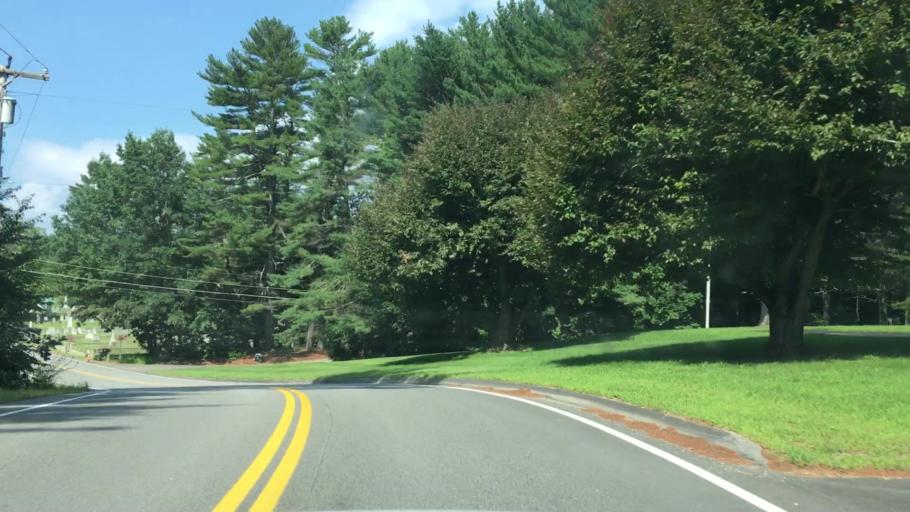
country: US
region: Maine
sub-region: Cumberland County
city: Raymond
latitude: 43.9019
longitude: -70.4610
